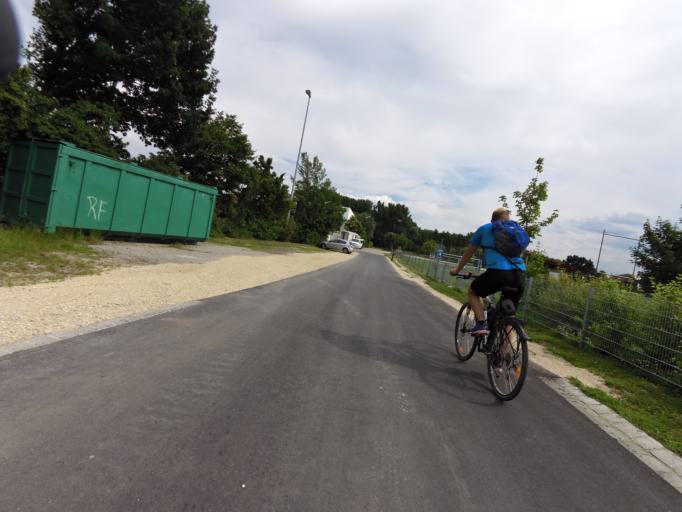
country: DE
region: Bavaria
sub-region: Upper Bavaria
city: Hebertshausen
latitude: 48.3041
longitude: 11.4945
